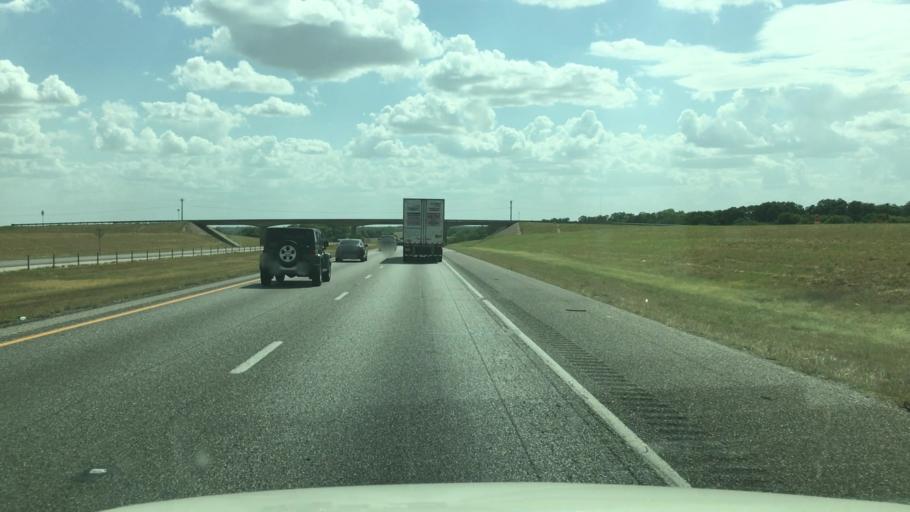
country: US
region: Texas
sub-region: Ellis County
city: Plum Grove
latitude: 32.1058
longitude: -97.0081
